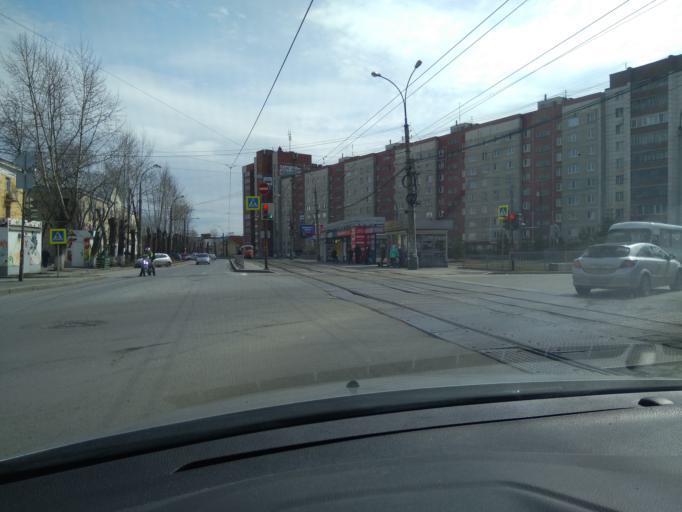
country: RU
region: Sverdlovsk
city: Shuvakish
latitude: 56.8718
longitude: 60.5204
